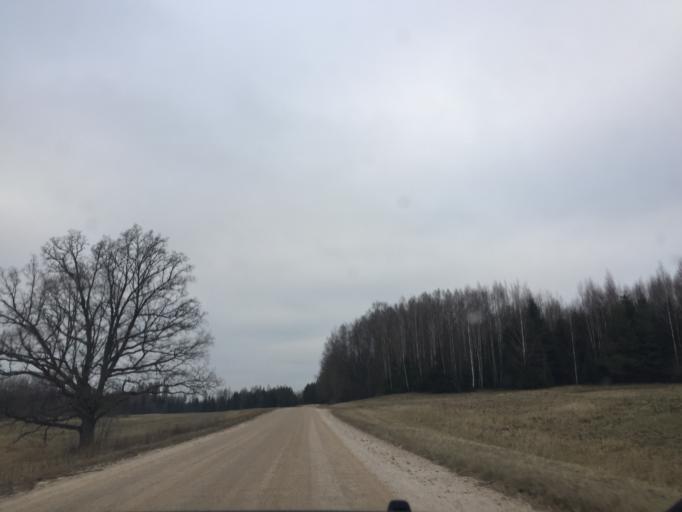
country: LV
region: Ligatne
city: Ligatne
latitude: 57.2108
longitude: 25.1339
